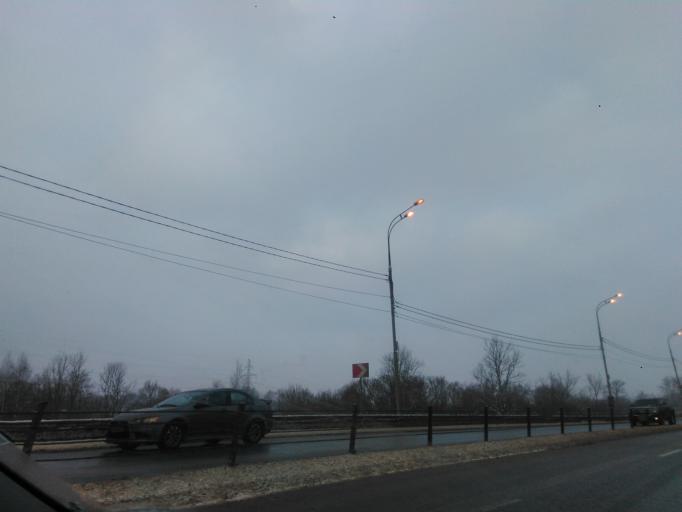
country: RU
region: Moskovskaya
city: Dedenevo
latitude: 56.2696
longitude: 37.5022
